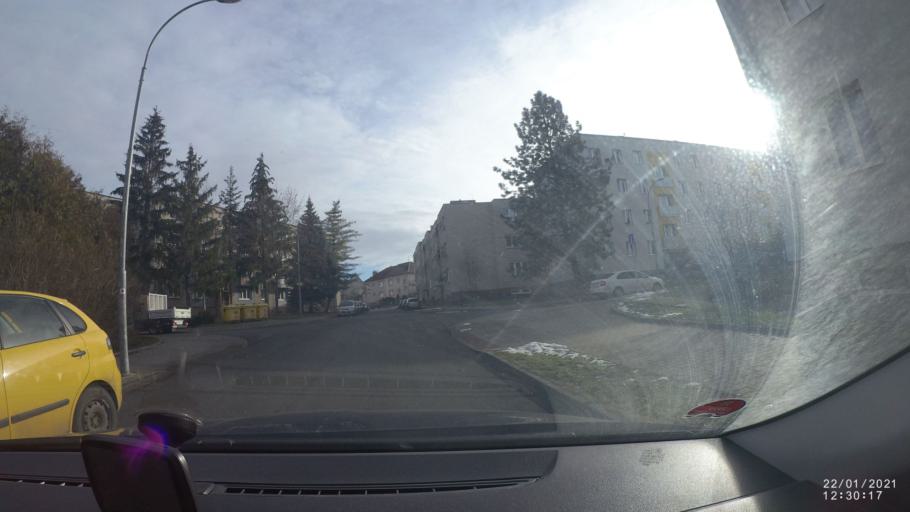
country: CZ
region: Plzensky
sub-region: Okres Plzen-Mesto
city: Pilsen
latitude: 49.7539
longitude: 13.4249
